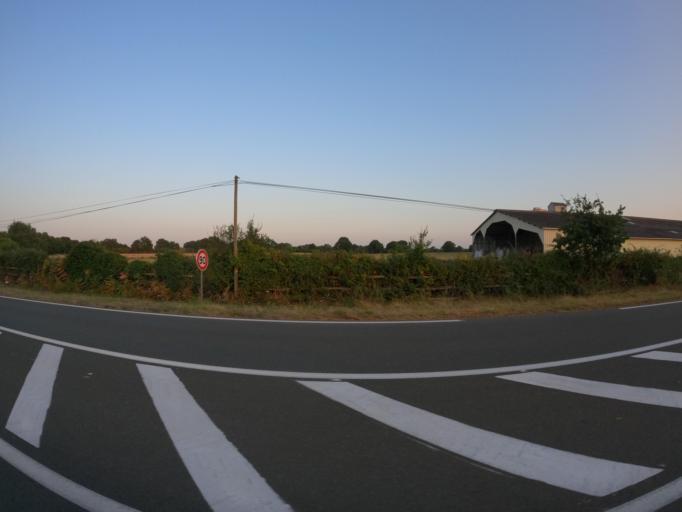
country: FR
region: Pays de la Loire
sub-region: Departement de la Mayenne
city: Aze
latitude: 47.8356
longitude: -0.6751
